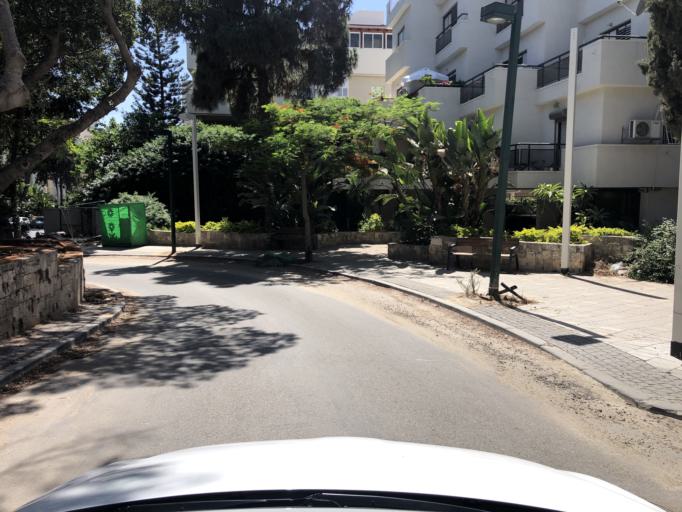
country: IL
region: Tel Aviv
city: Ramat Gan
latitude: 32.0787
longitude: 34.8060
